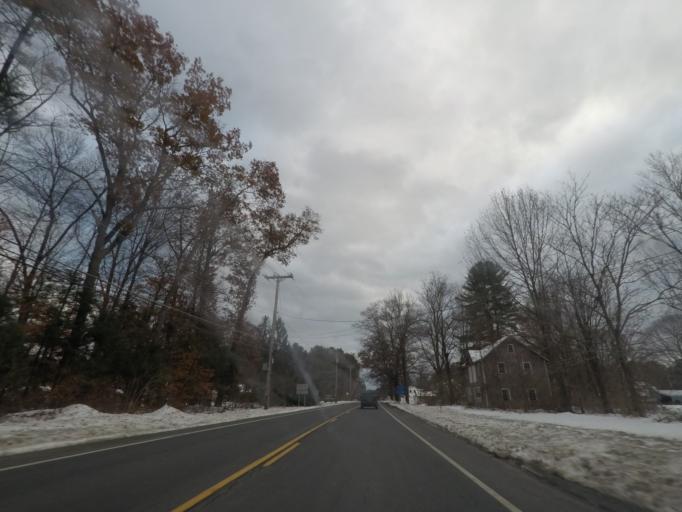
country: US
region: New York
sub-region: Ulster County
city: Tillson
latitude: 41.8340
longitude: -74.0698
